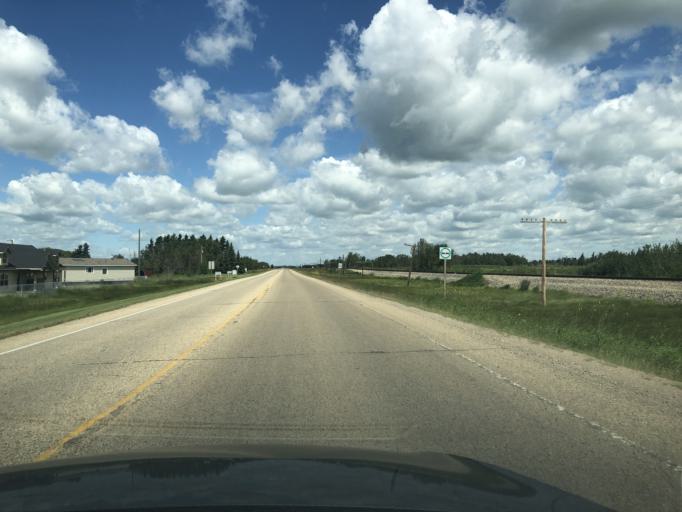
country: CA
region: Alberta
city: Millet
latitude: 53.0982
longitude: -113.4728
